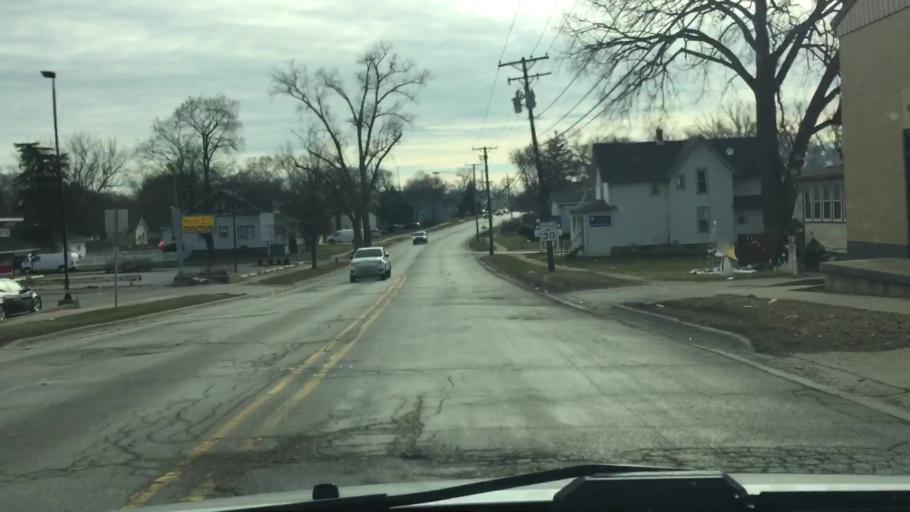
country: US
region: Illinois
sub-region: Kane County
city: Elgin
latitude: 42.0187
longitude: -88.2685
